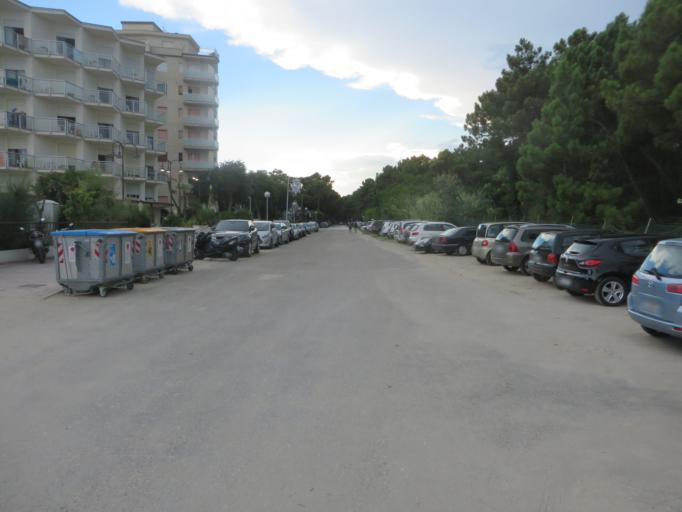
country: IT
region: Emilia-Romagna
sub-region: Provincia di Ravenna
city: Cervia
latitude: 44.2933
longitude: 12.3481
